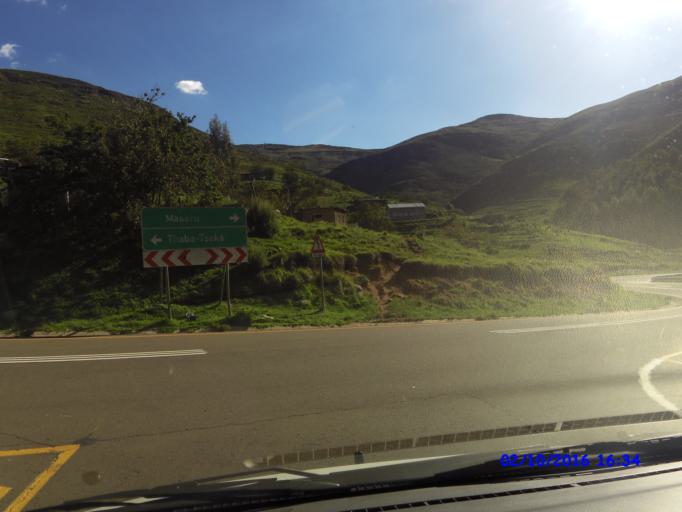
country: LS
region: Maseru
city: Nako
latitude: -29.4931
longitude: 28.0596
